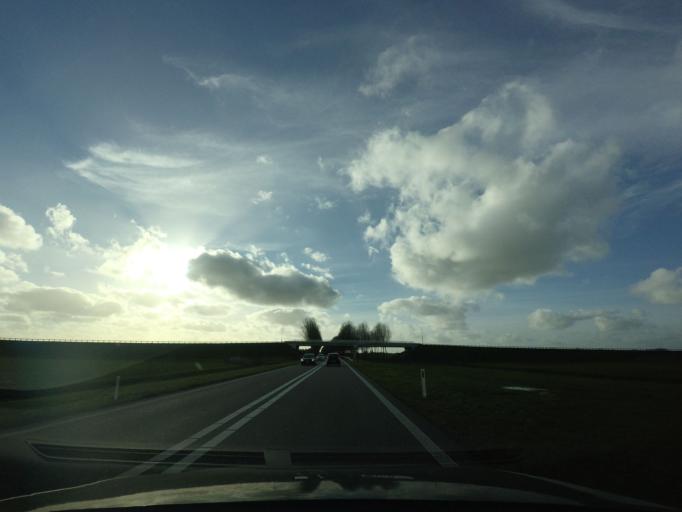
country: NL
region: North Holland
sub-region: Gemeente Opmeer
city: Opmeer
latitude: 52.7551
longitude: 4.9286
